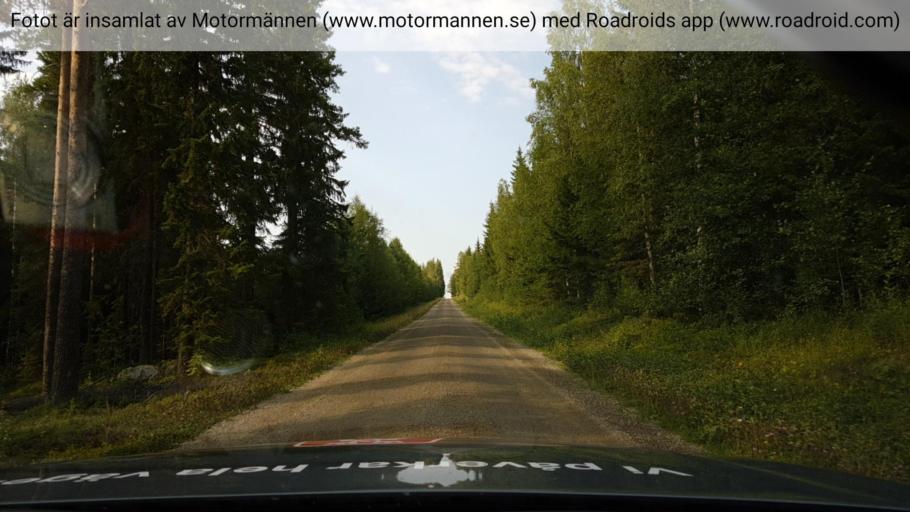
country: SE
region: Jaemtland
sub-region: Braecke Kommun
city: Braecke
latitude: 62.5082
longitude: 14.9176
